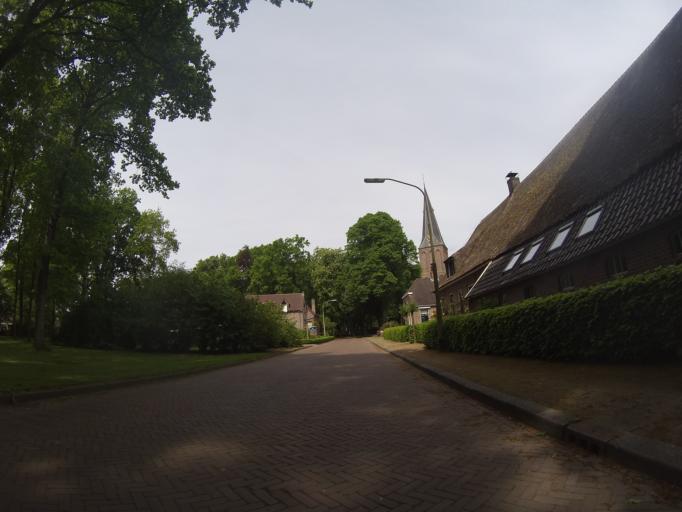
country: NL
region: Drenthe
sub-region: Gemeente Coevorden
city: Sleen
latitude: 52.7751
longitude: 6.8037
